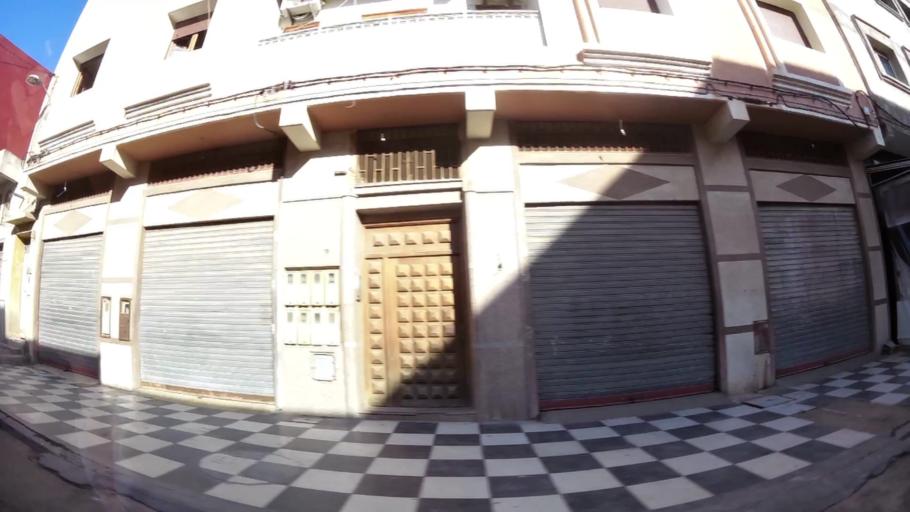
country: MA
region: Oriental
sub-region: Oujda-Angad
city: Oujda
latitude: 34.6934
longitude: -1.9176
